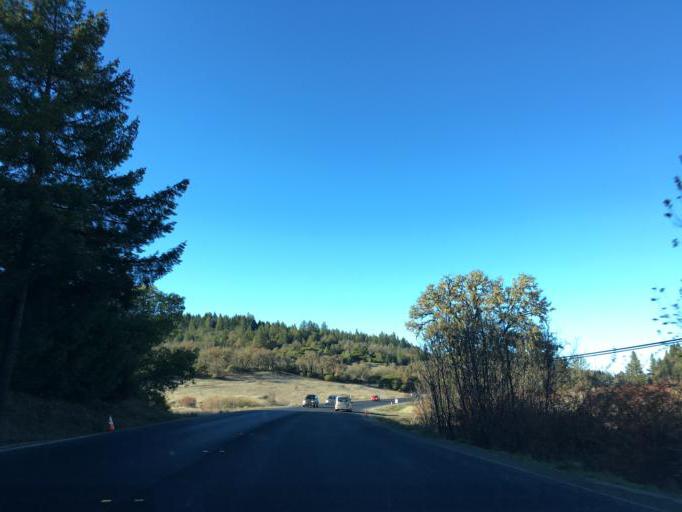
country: US
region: California
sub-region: Mendocino County
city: Laytonville
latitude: 39.6327
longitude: -123.4662
